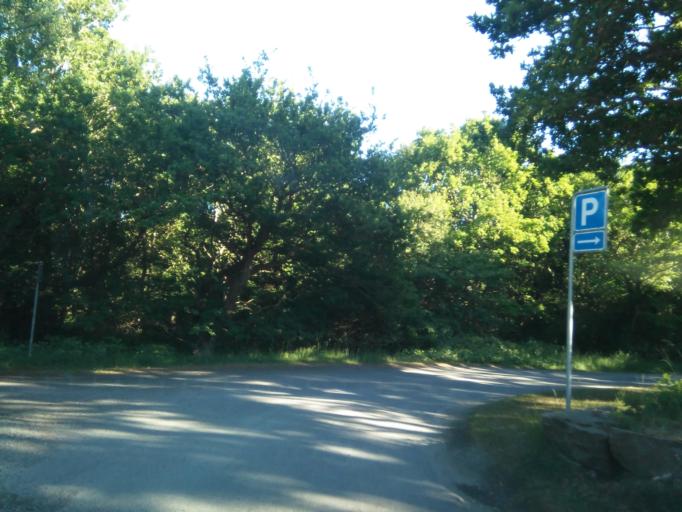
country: DK
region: Capital Region
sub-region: Bornholm Kommune
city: Ronne
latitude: 55.2805
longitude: 14.7603
